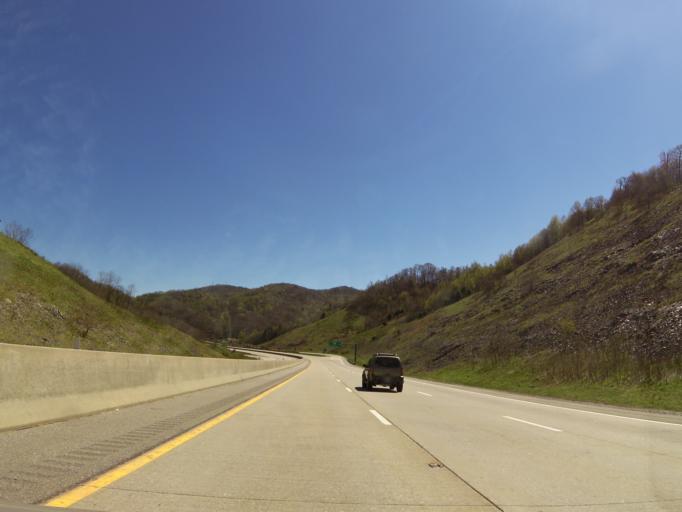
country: US
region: North Carolina
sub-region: Madison County
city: Mars Hill
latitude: 35.9149
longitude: -82.5583
